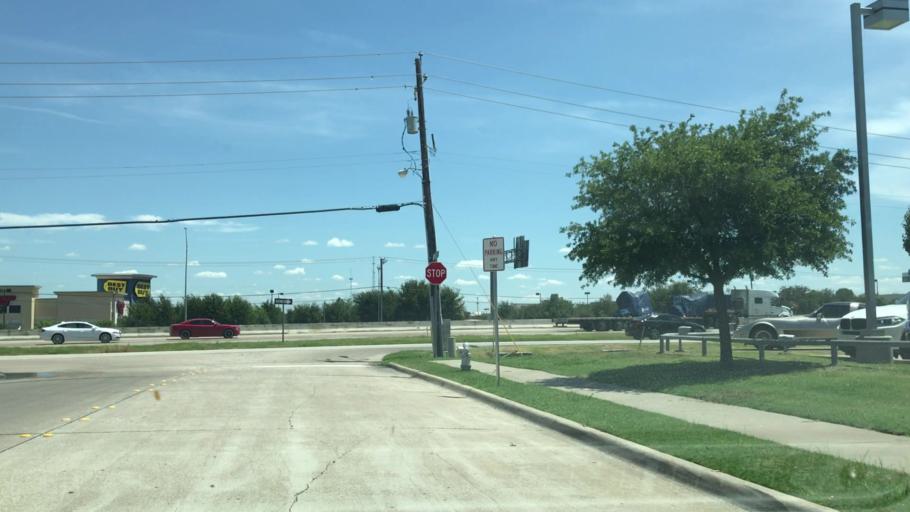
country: US
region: Texas
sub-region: Rockwall County
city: Rockwall
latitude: 32.9048
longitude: -96.4548
